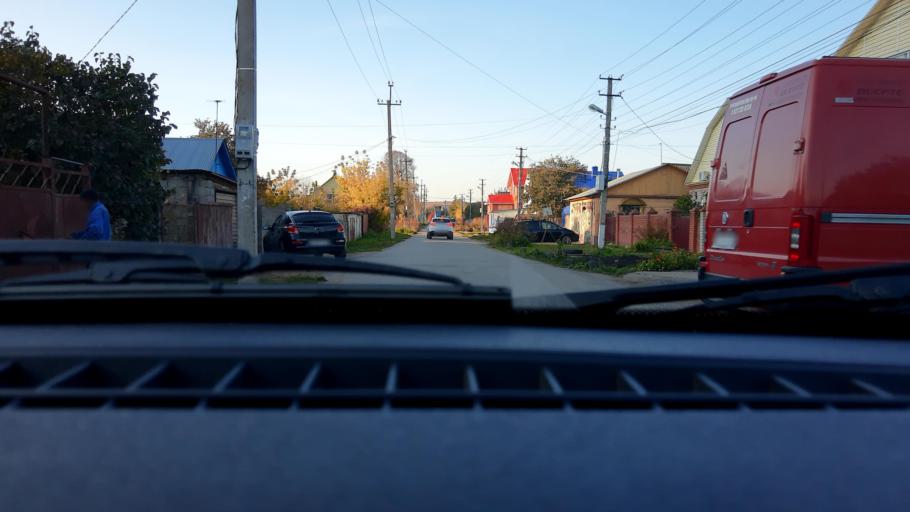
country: RU
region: Bashkortostan
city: Mikhaylovka
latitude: 54.7900
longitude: 55.8873
